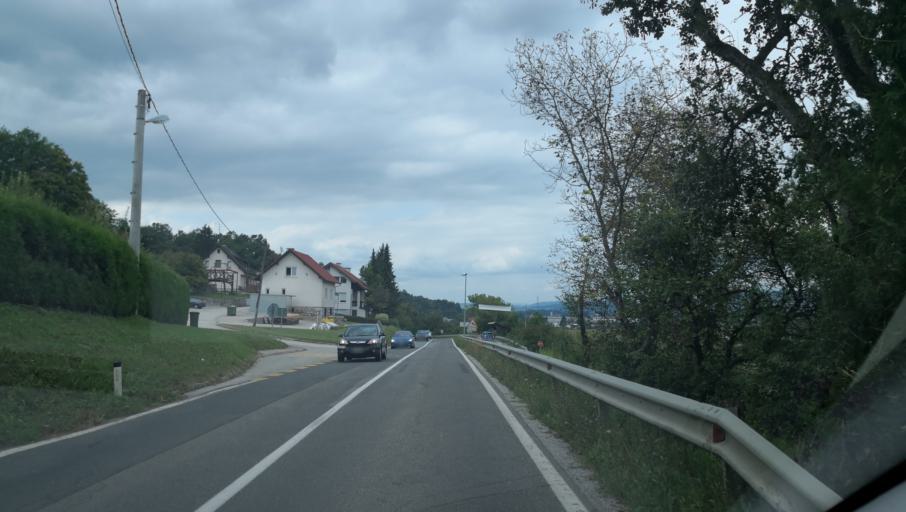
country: SI
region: Novo Mesto
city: Novo Mesto
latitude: 45.7748
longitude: 15.1873
